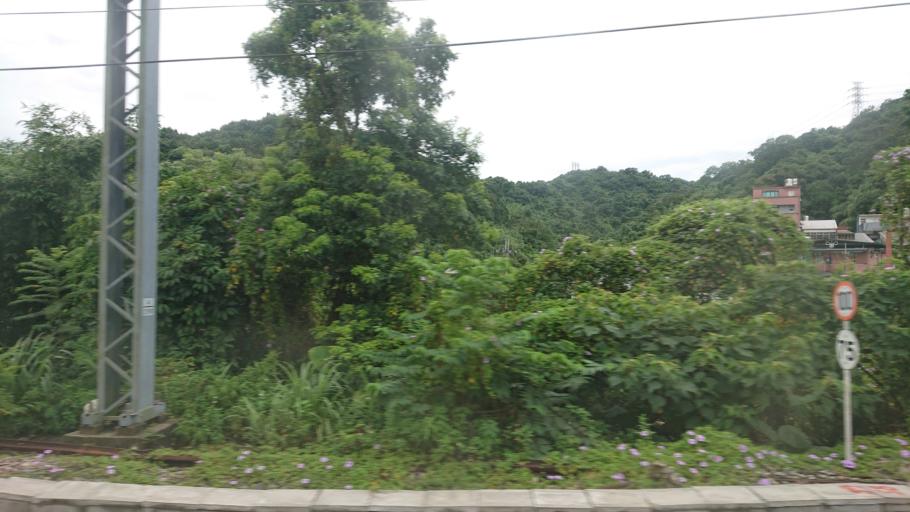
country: TW
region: Taiwan
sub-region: Keelung
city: Keelung
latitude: 25.1028
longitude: 121.7252
